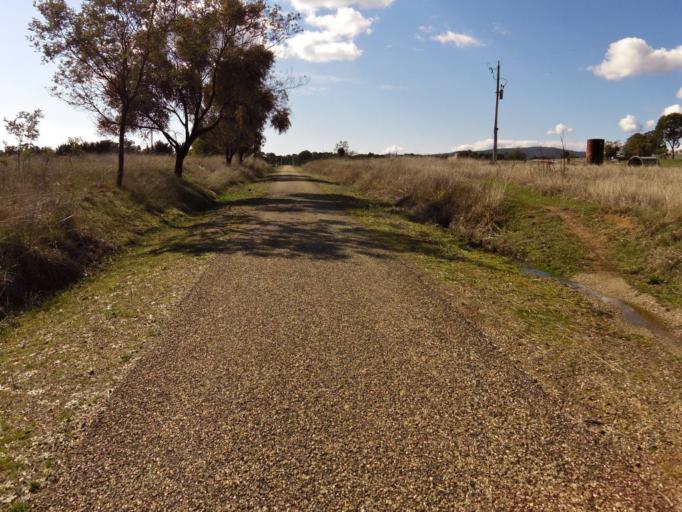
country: AU
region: Victoria
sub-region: Wangaratta
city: Wangaratta
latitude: -36.3954
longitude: 146.6562
